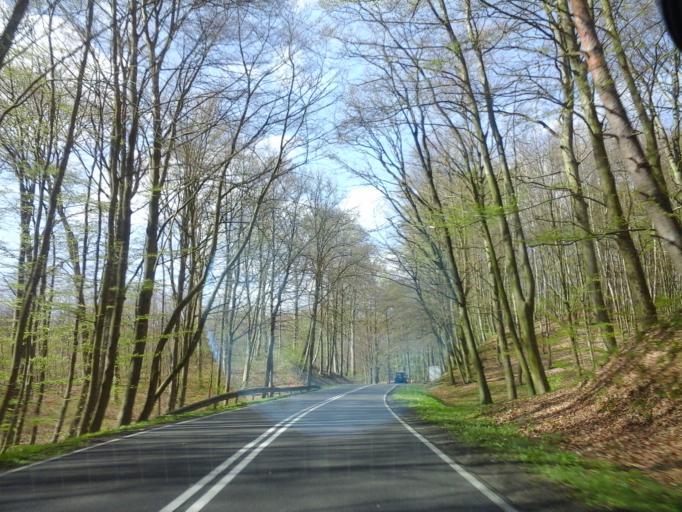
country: PL
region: West Pomeranian Voivodeship
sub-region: Powiat stargardzki
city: Suchan
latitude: 53.2634
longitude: 15.3301
